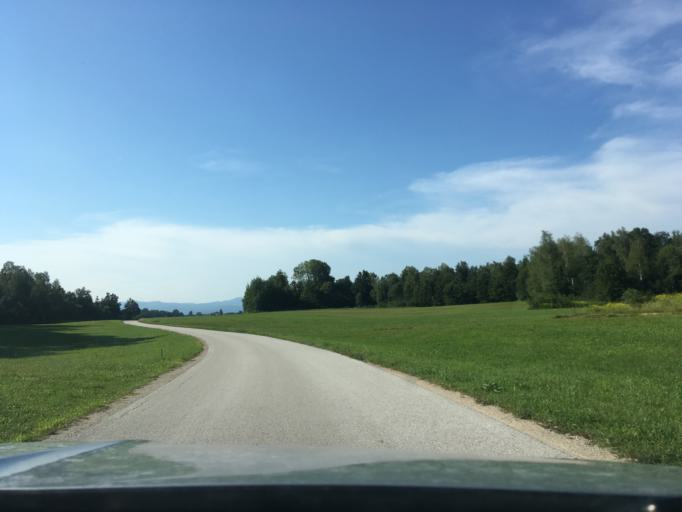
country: SI
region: Crnomelj
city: Crnomelj
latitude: 45.4584
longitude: 15.2163
